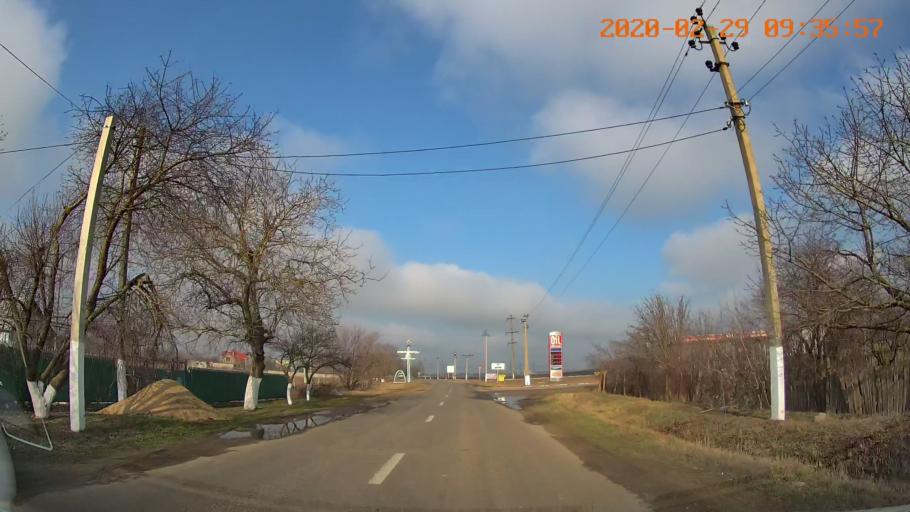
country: MD
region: Telenesti
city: Dnestrovsc
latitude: 46.6219
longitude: 29.8942
